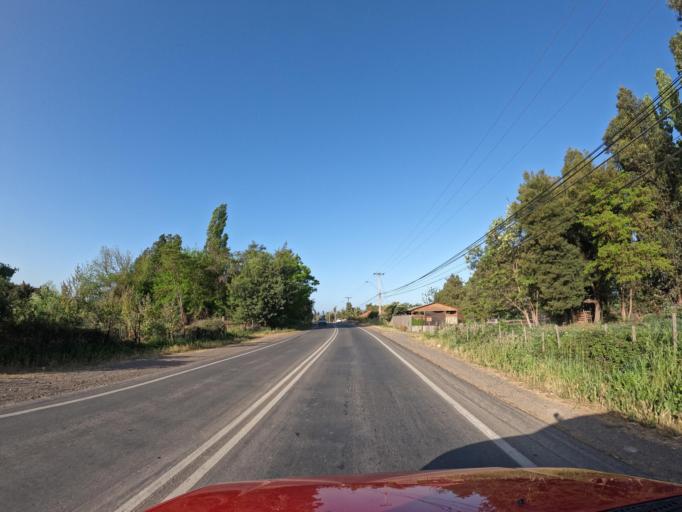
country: CL
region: O'Higgins
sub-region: Provincia de Colchagua
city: Santa Cruz
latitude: -34.5252
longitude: -71.3848
